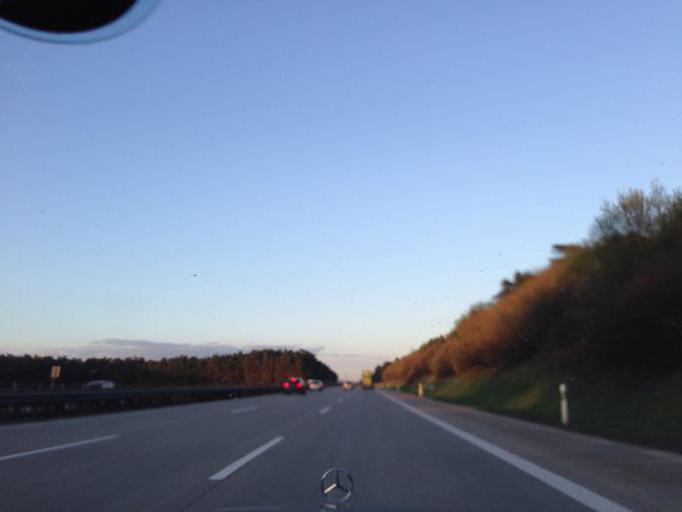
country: DE
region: Lower Saxony
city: Egestorf
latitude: 53.1501
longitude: 10.0333
